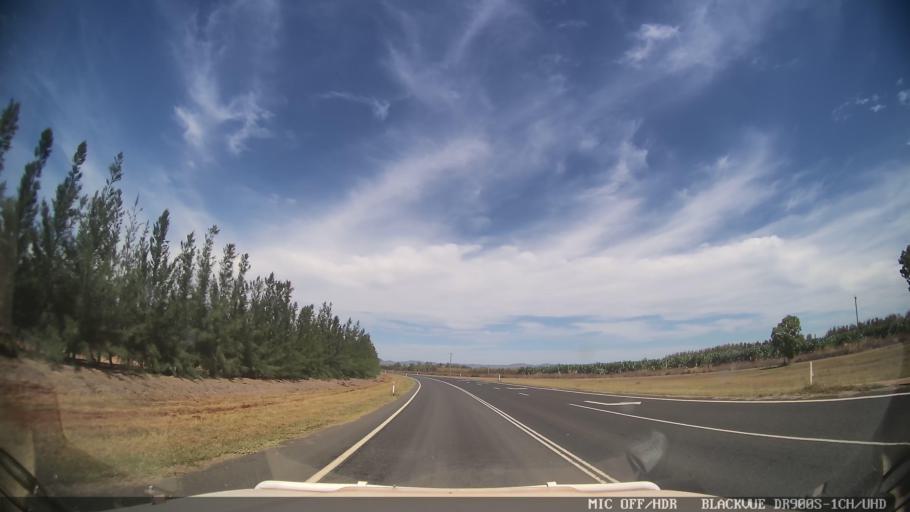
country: AU
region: Queensland
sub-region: Cook
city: Cooktown
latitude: -15.8359
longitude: 144.8540
